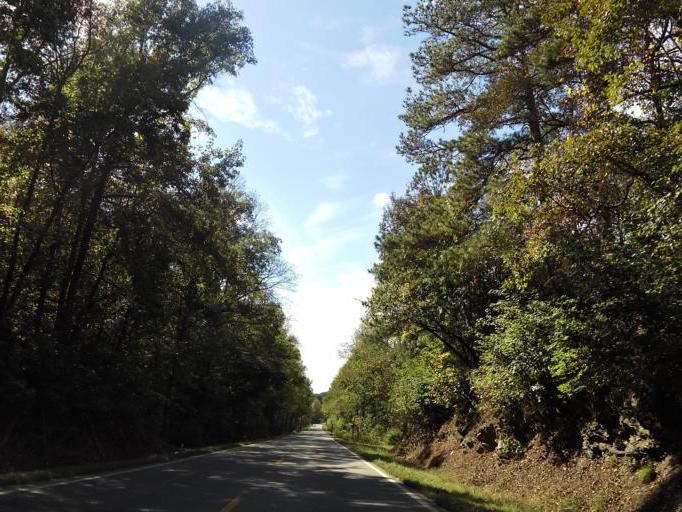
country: US
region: Georgia
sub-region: Pickens County
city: Nelson
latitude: 34.4119
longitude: -84.3937
